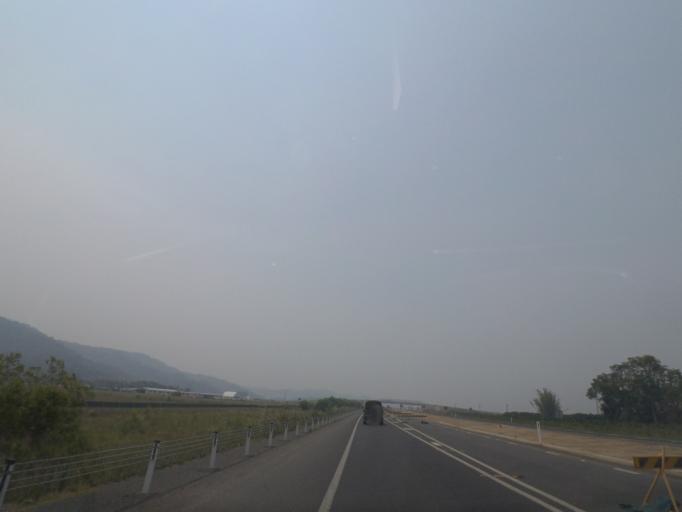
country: AU
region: New South Wales
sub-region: Ballina
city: Ballina
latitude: -28.9062
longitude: 153.4789
